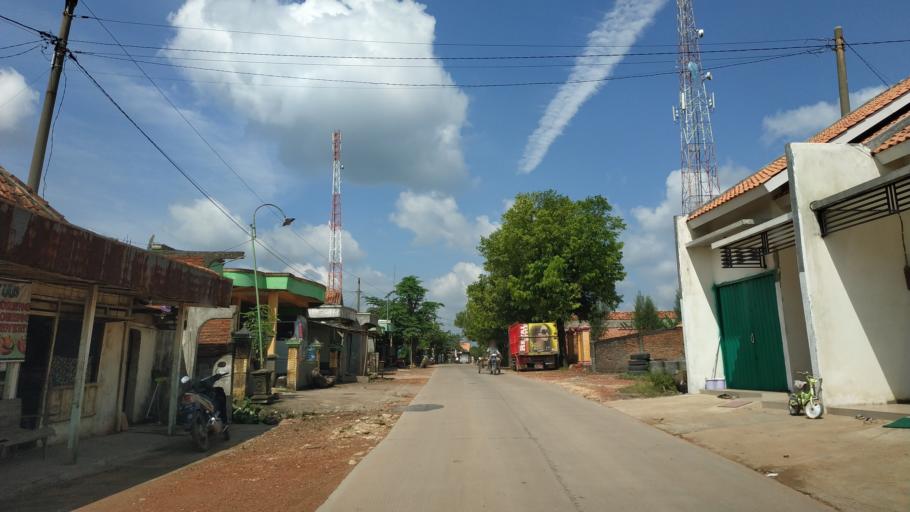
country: ID
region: Central Java
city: Jepang
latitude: -7.0088
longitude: 111.1147
